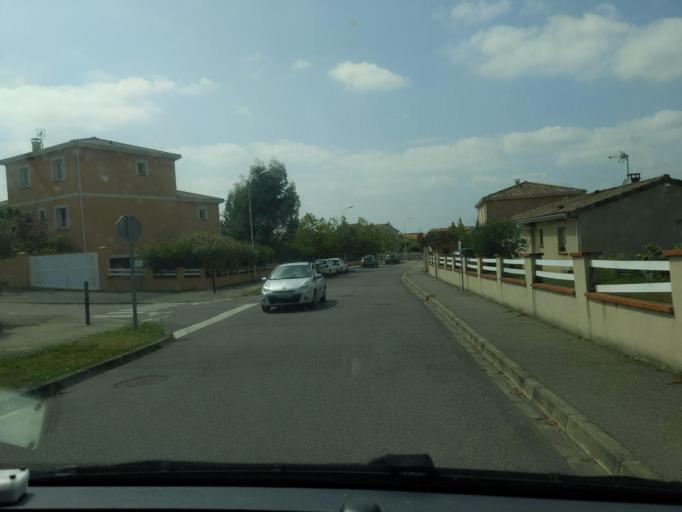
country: FR
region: Midi-Pyrenees
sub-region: Departement de la Haute-Garonne
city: Balma
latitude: 43.6119
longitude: 1.5179
